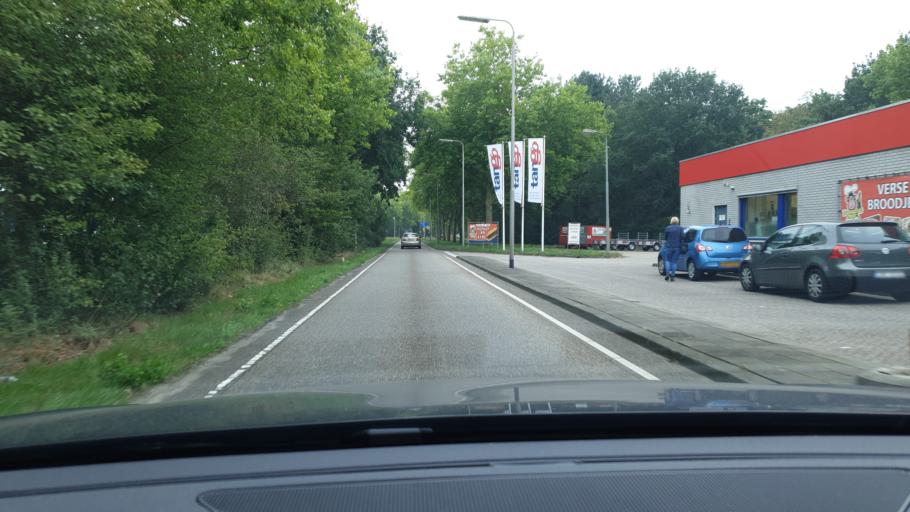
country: NL
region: North Brabant
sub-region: Gemeente Oss
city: Oss
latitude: 51.7548
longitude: 5.5254
